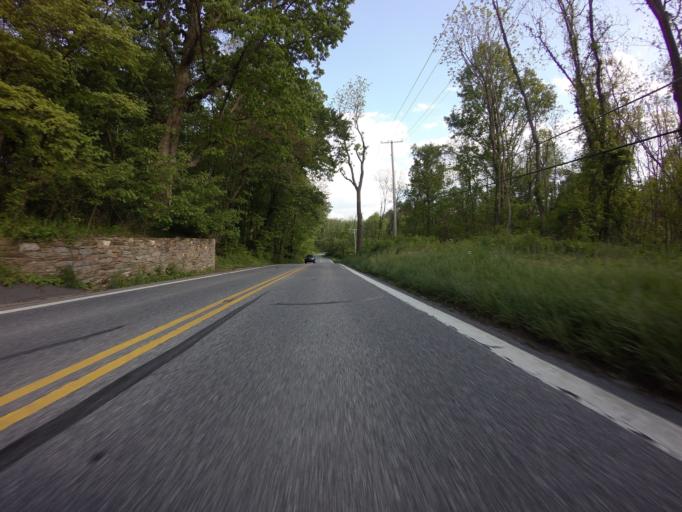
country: US
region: Maryland
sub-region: Baltimore County
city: Hunt Valley
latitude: 39.5044
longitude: -76.7117
